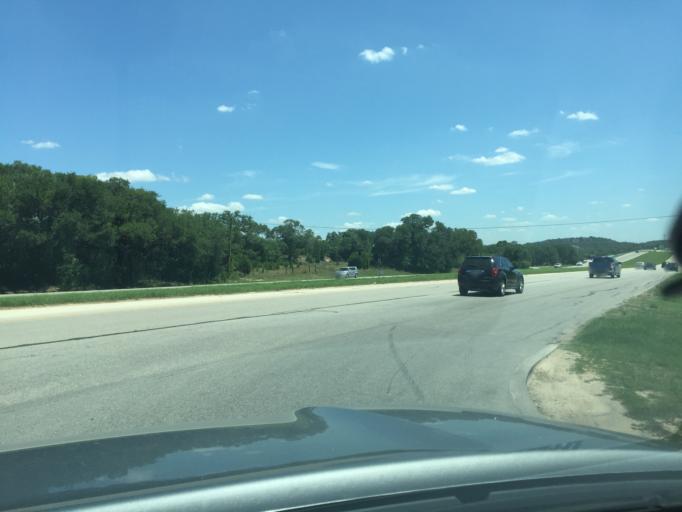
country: US
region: Texas
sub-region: Comal County
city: Bulverde
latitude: 29.8025
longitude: -98.4181
